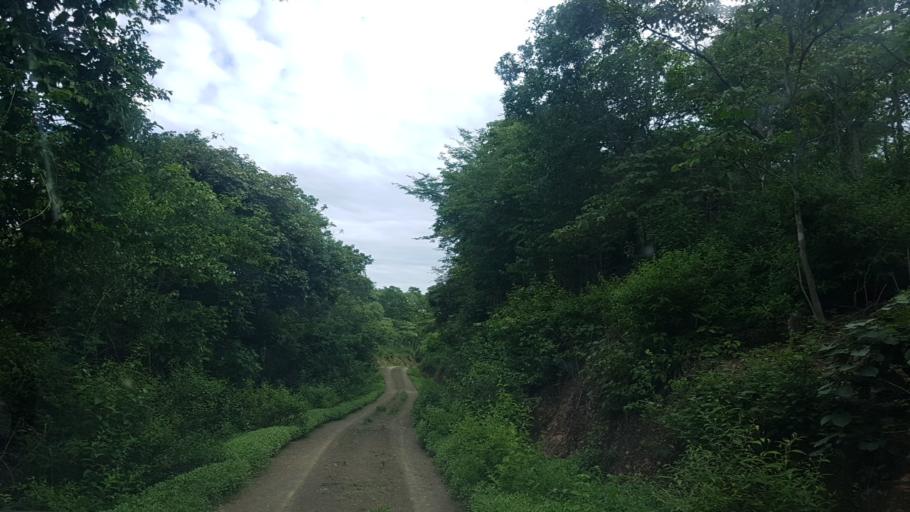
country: NI
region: Nueva Segovia
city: Ciudad Antigua
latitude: 13.5978
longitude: -86.3672
